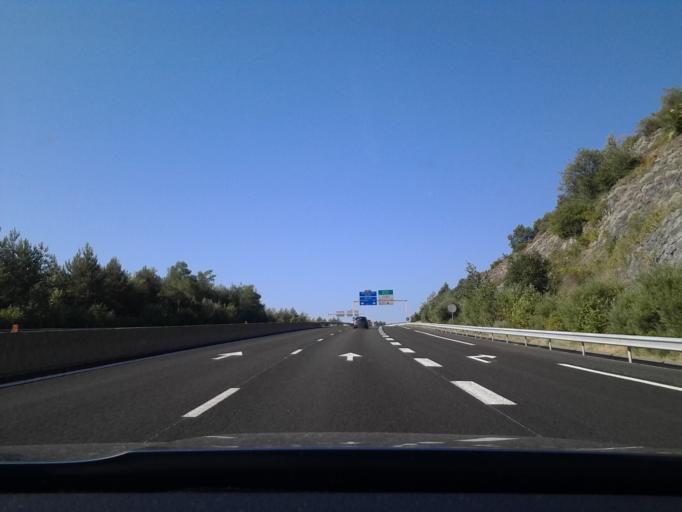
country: FR
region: Languedoc-Roussillon
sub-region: Departement de la Lozere
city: Chirac
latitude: 44.5046
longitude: 3.2435
